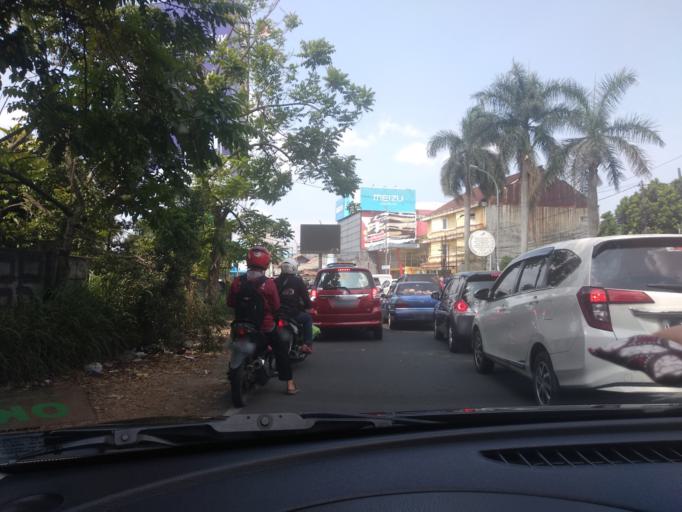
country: ID
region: West Java
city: Bandung
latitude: -6.8923
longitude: 107.5805
